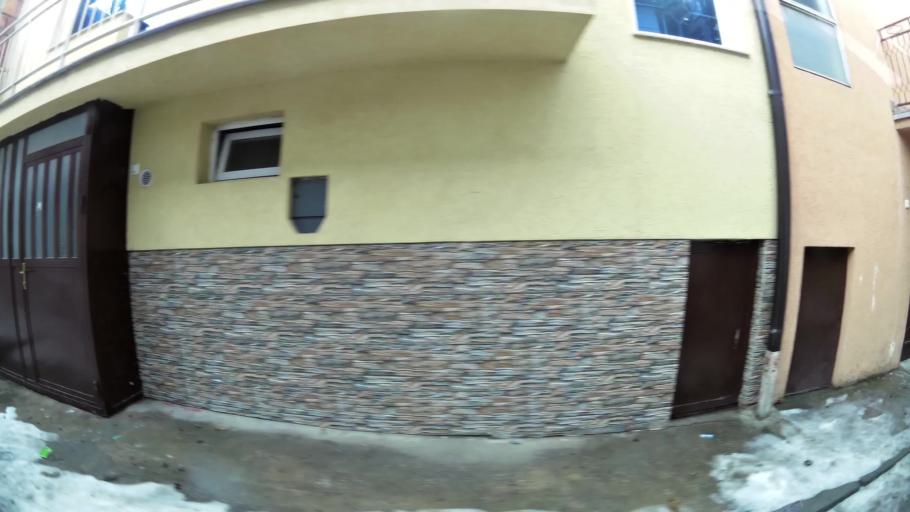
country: XK
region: Pristina
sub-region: Komuna e Prishtines
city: Pristina
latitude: 42.6709
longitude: 21.1725
